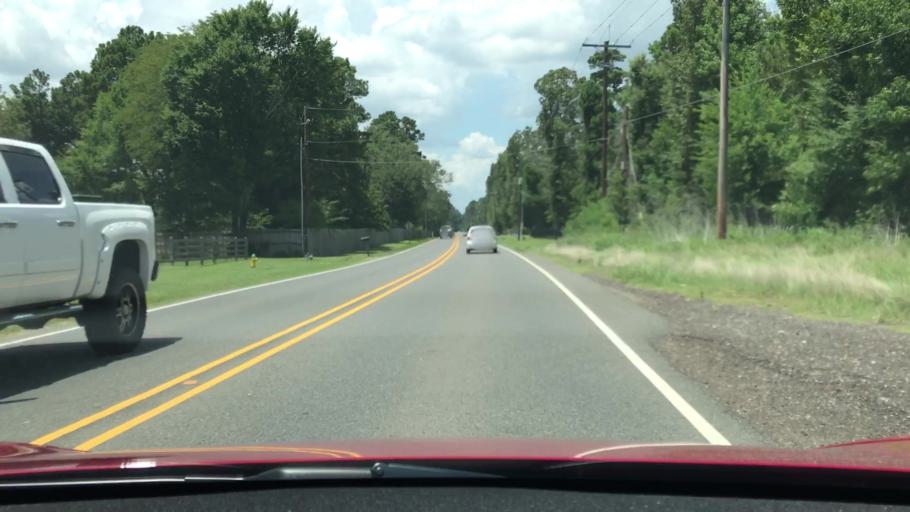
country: US
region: Louisiana
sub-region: De Soto Parish
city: Stonewall
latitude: 32.3652
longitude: -93.6935
